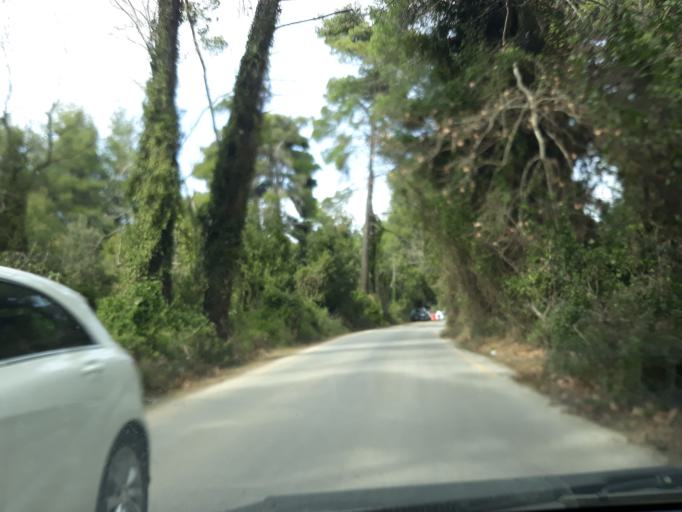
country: GR
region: Attica
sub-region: Nomarchia Anatolikis Attikis
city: Varybobi
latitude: 38.1584
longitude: 23.7916
